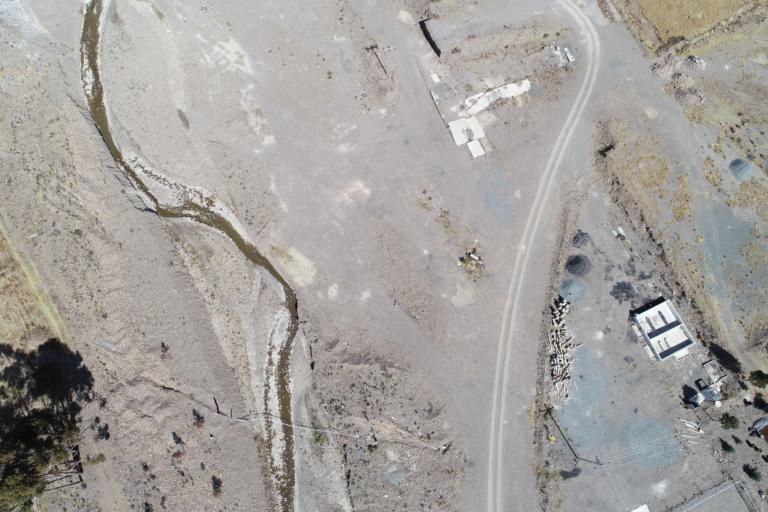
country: BO
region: La Paz
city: Achacachi
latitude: -15.9008
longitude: -68.9045
